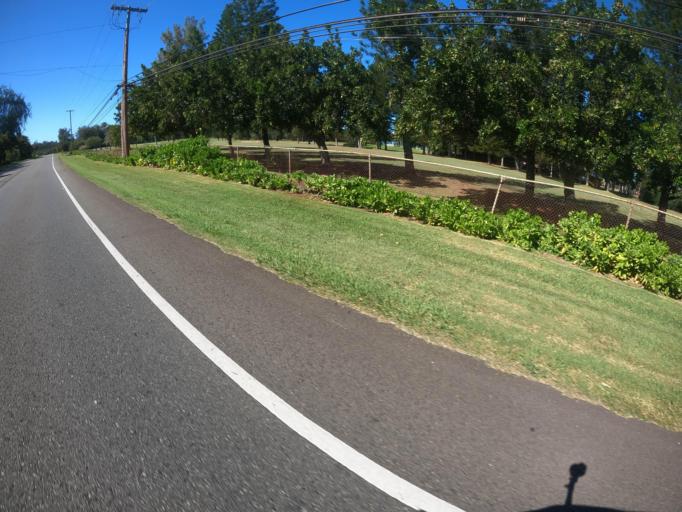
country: US
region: Hawaii
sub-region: Honolulu County
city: Kahuku
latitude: 21.6963
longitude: -157.9984
